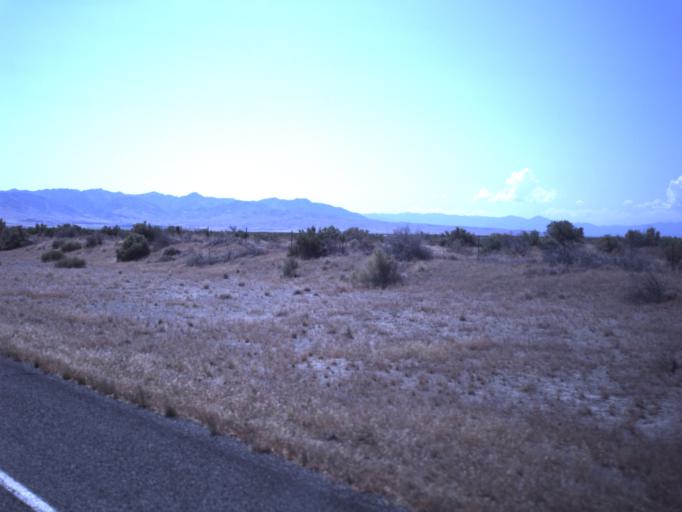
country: US
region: Utah
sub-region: Millard County
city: Delta
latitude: 39.4762
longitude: -112.4893
